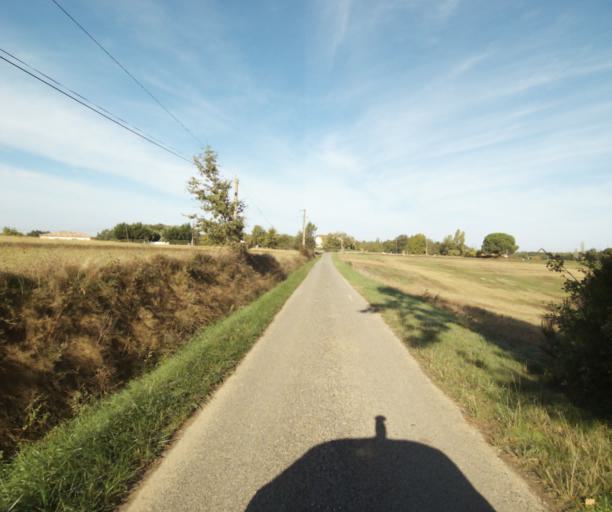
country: FR
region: Midi-Pyrenees
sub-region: Departement du Tarn-et-Garonne
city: Nohic
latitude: 43.9263
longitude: 1.4653
